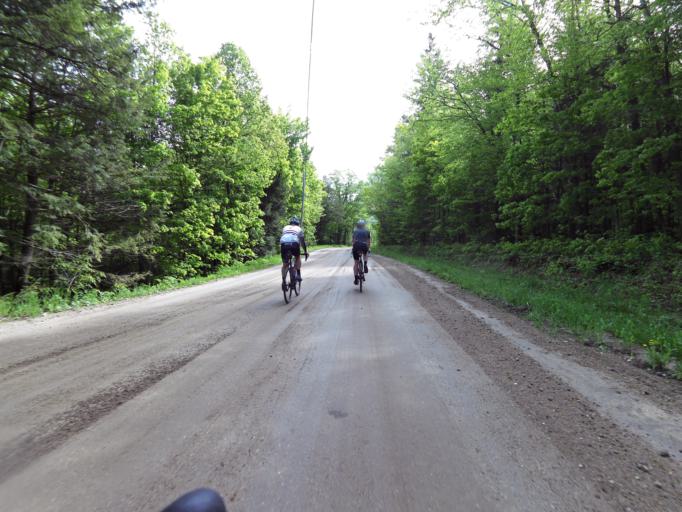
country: CA
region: Quebec
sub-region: Outaouais
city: Wakefield
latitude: 45.7066
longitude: -75.8972
